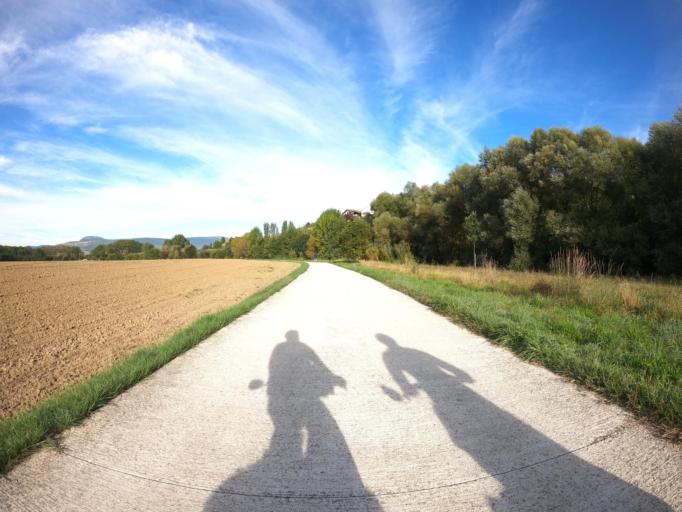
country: ES
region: Navarre
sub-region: Provincia de Navarra
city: Orkoien
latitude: 42.8145
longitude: -1.7219
